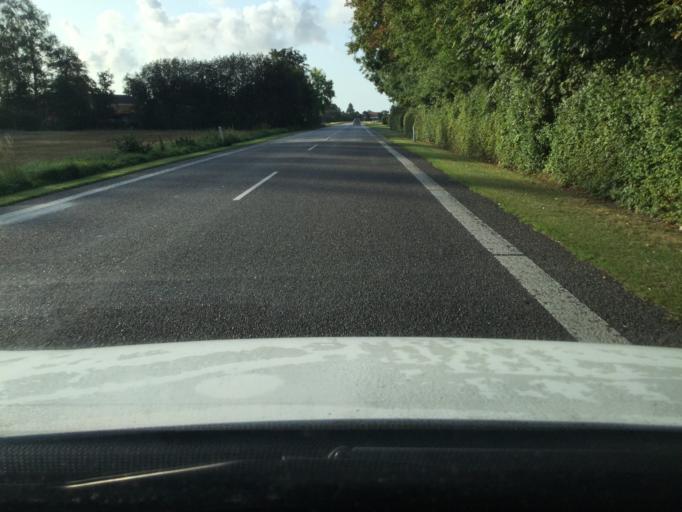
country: DK
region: Zealand
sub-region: Lolland Kommune
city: Rodby
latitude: 54.7803
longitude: 11.2958
